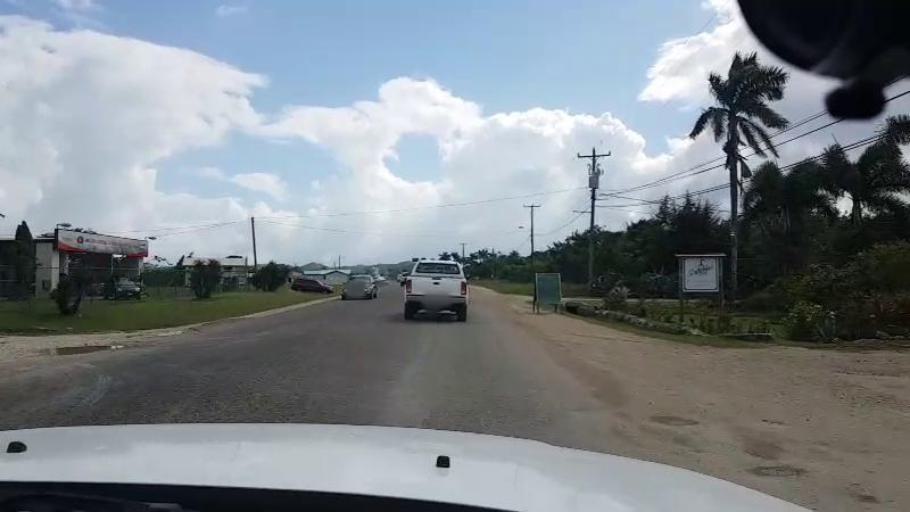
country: BZ
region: Cayo
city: Belmopan
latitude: 17.2438
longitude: -88.7831
